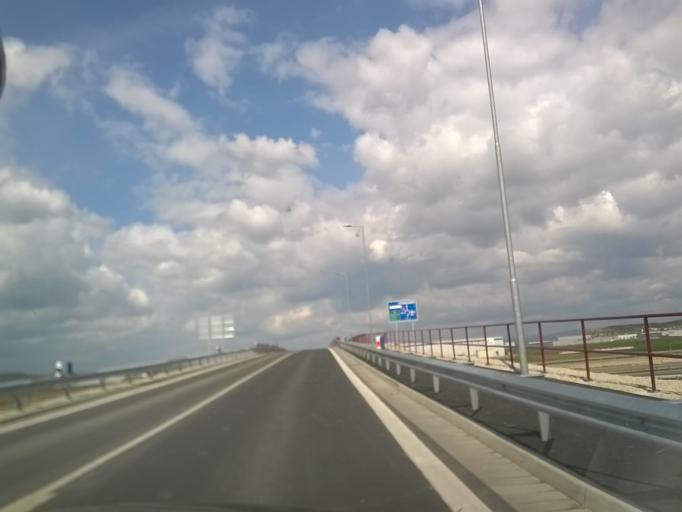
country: SK
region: Nitriansky
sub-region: Okres Nitra
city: Nitra
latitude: 48.3257
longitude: 18.0643
